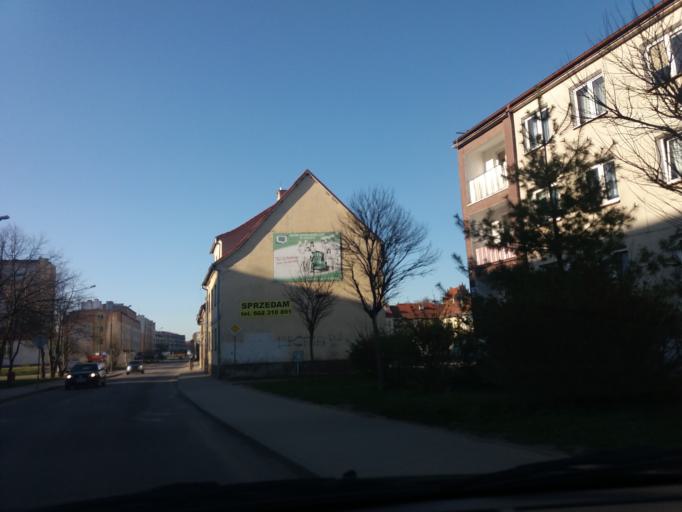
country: PL
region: Warmian-Masurian Voivodeship
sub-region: Powiat nidzicki
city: Nidzica
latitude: 53.3559
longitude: 20.4262
